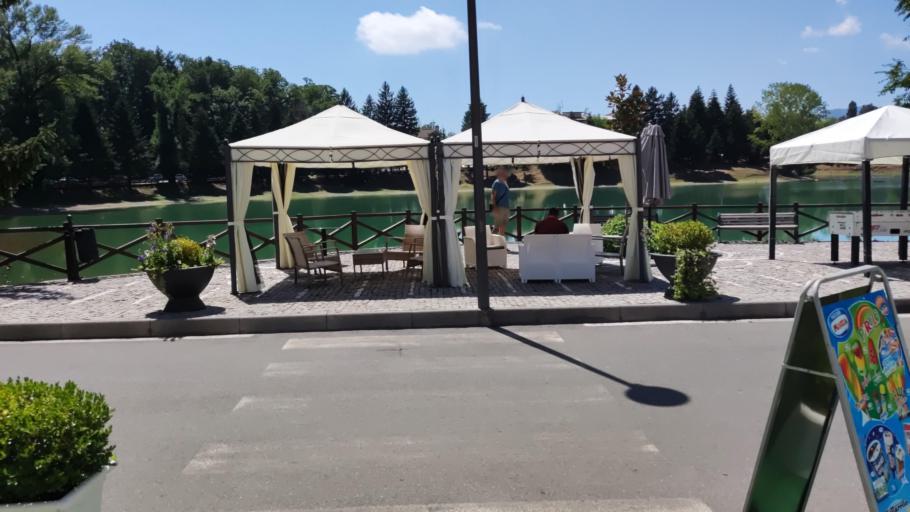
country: IT
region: Basilicate
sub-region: Provincia di Potenza
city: Nemoli
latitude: 40.0923
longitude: 15.8103
